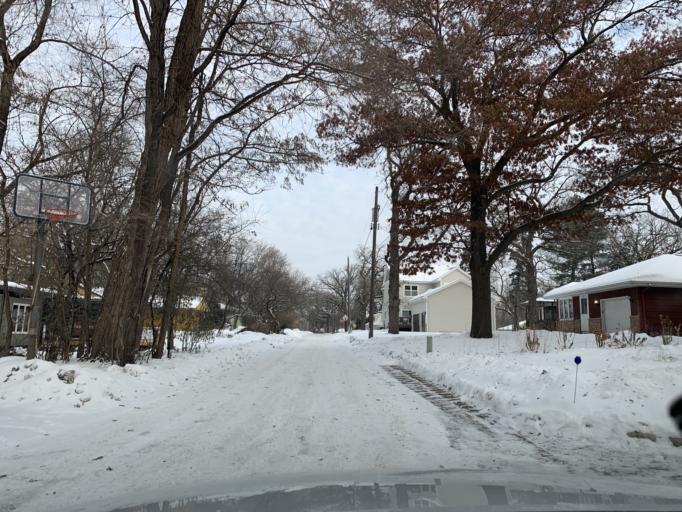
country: US
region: Minnesota
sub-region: Hennepin County
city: Saint Louis Park
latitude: 44.9215
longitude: -93.3555
